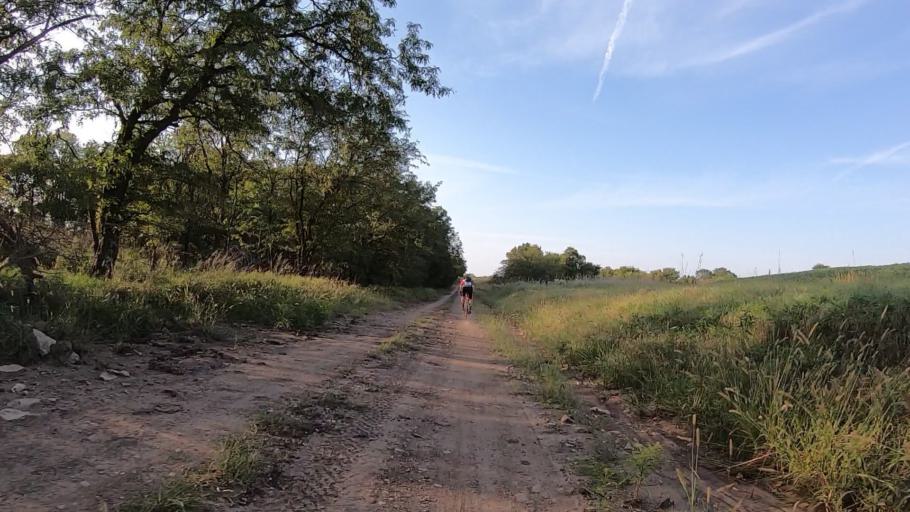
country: US
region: Kansas
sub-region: Marshall County
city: Blue Rapids
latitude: 39.7616
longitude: -96.7508
